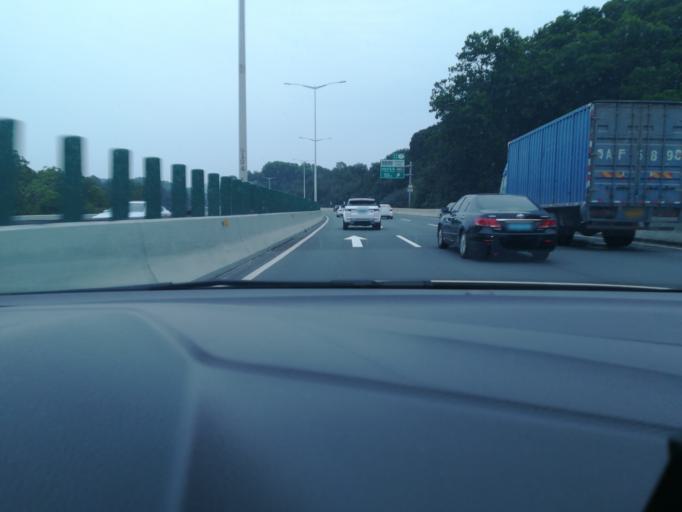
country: CN
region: Guangdong
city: Taihe
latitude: 23.2686
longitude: 113.3621
